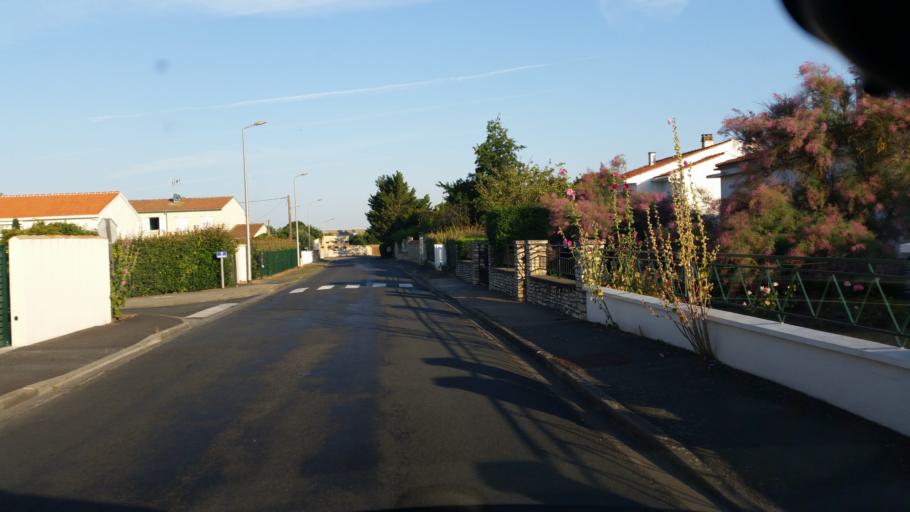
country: FR
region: Poitou-Charentes
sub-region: Departement de la Charente-Maritime
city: Marans
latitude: 46.3073
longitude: -0.9984
